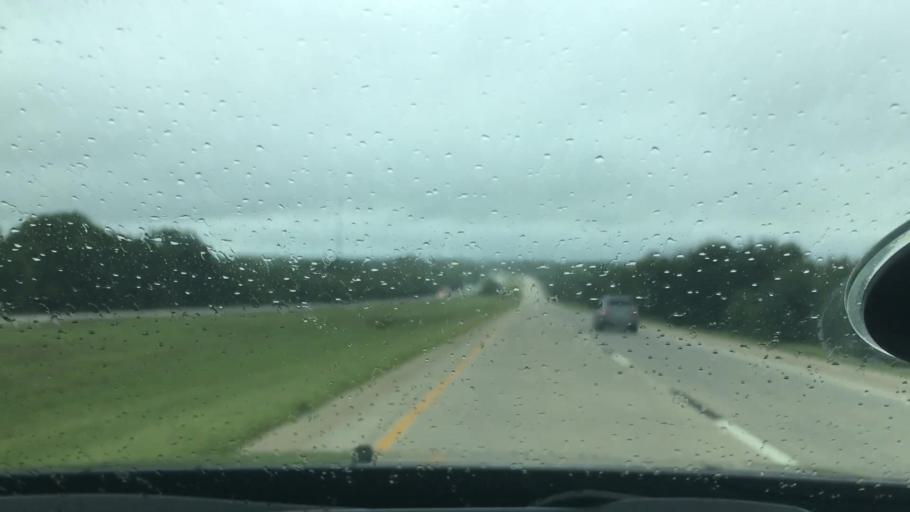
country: US
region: Oklahoma
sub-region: Okmulgee County
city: Henryetta
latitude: 35.4310
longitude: -95.9208
